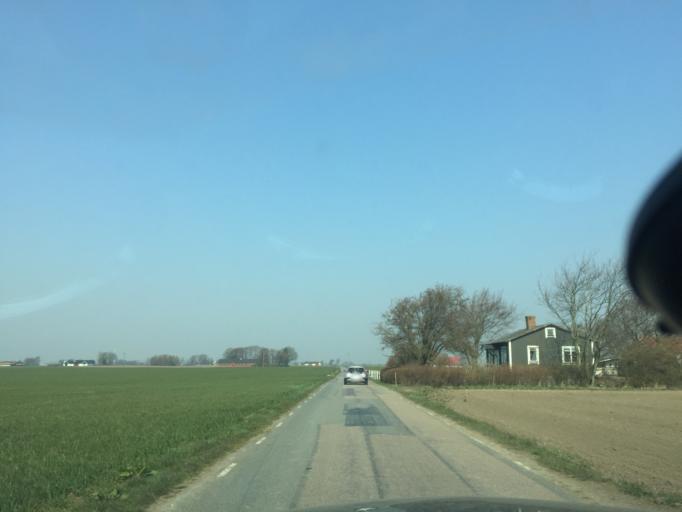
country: SE
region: Skane
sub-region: Simrishamns Kommun
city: Simrishamn
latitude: 55.4482
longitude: 14.2171
